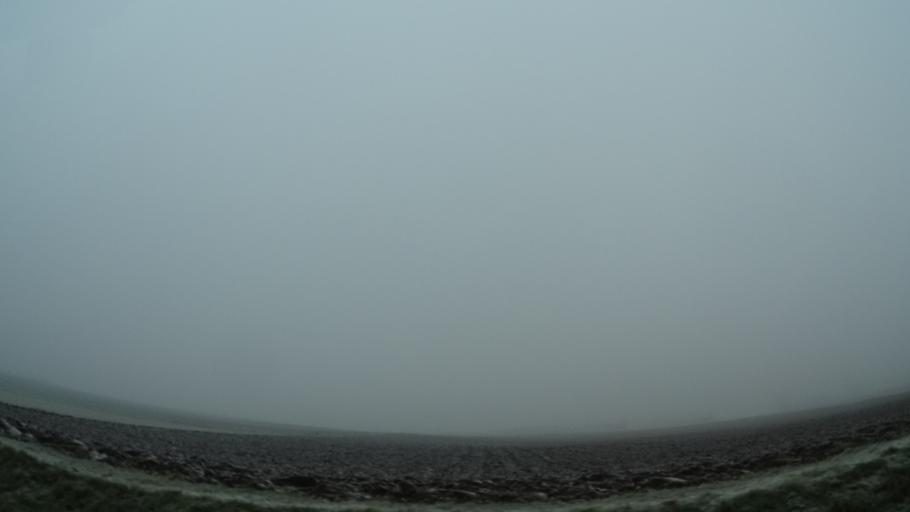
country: DE
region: Bavaria
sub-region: Regierungsbezirk Unterfranken
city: Dingolshausen
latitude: 49.9115
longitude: 10.3894
